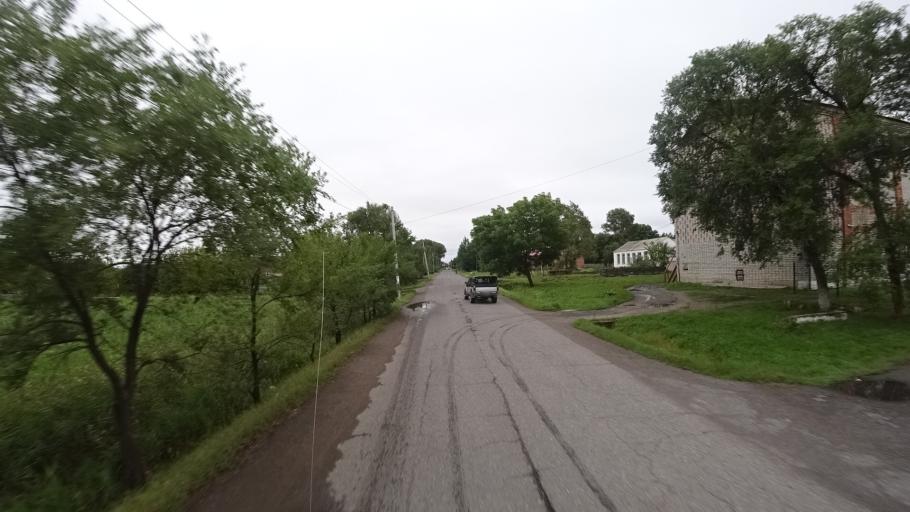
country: RU
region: Primorskiy
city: Chernigovka
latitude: 44.3390
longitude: 132.5780
